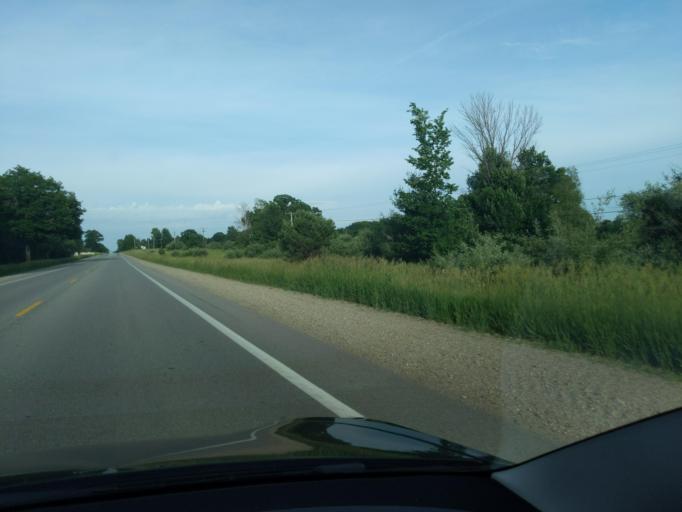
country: US
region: Michigan
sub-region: Montcalm County
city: Lakeview
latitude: 43.4313
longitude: -85.2505
